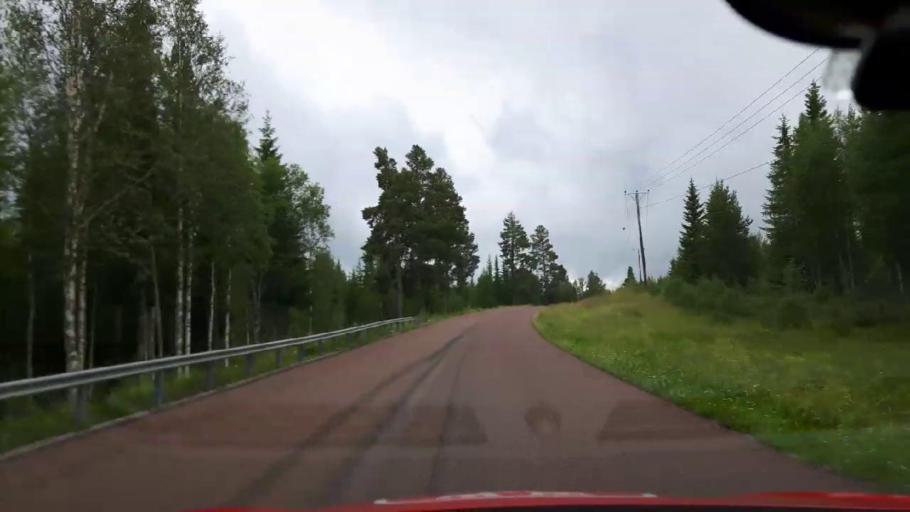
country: SE
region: Jaemtland
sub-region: Krokoms Kommun
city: Valla
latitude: 63.3456
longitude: 13.7225
